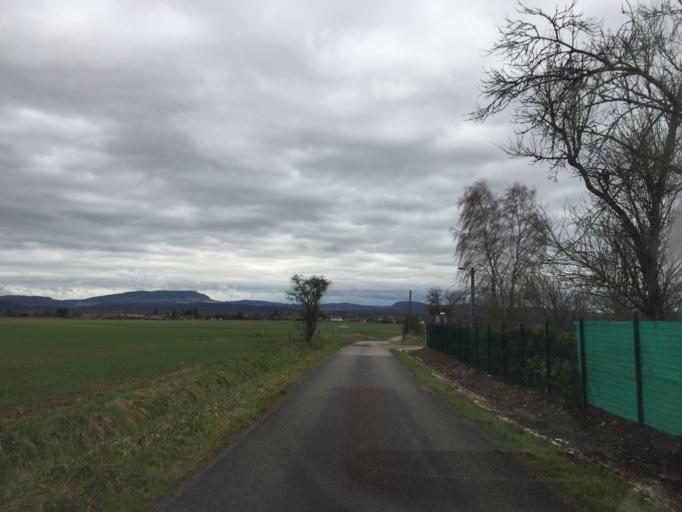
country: FR
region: Franche-Comte
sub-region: Departement du Doubs
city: Arc-et-Senans
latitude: 47.0289
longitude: 5.7059
